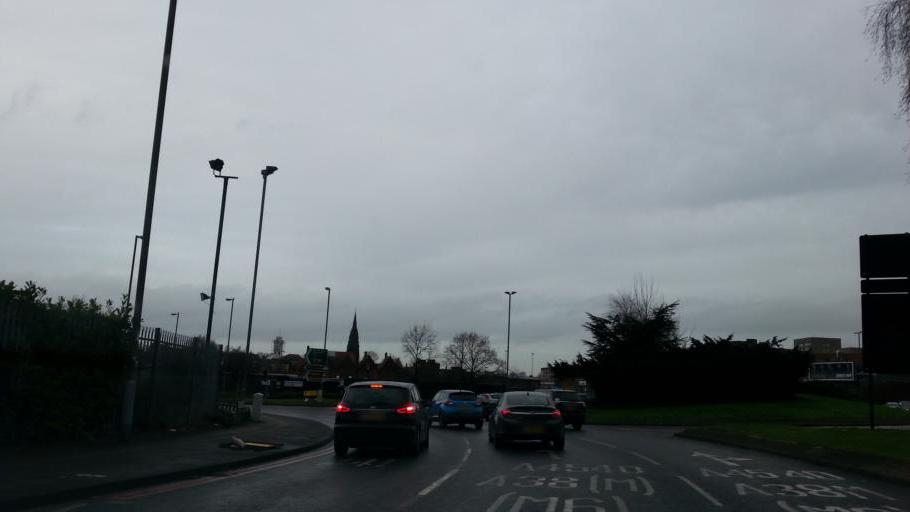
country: GB
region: England
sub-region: City and Borough of Birmingham
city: Hockley
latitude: 52.4916
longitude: -1.9158
